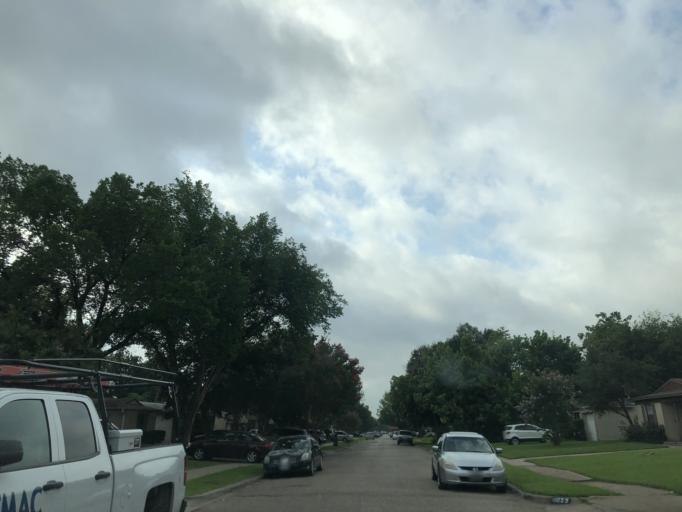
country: US
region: Texas
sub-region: Dallas County
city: Garland
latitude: 32.8340
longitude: -96.6442
